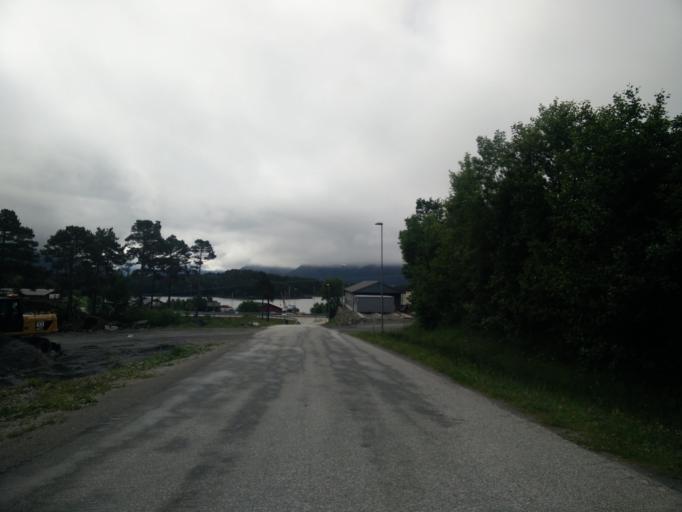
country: NO
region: More og Romsdal
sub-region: Kristiansund
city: Rensvik
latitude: 63.0127
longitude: 7.9690
